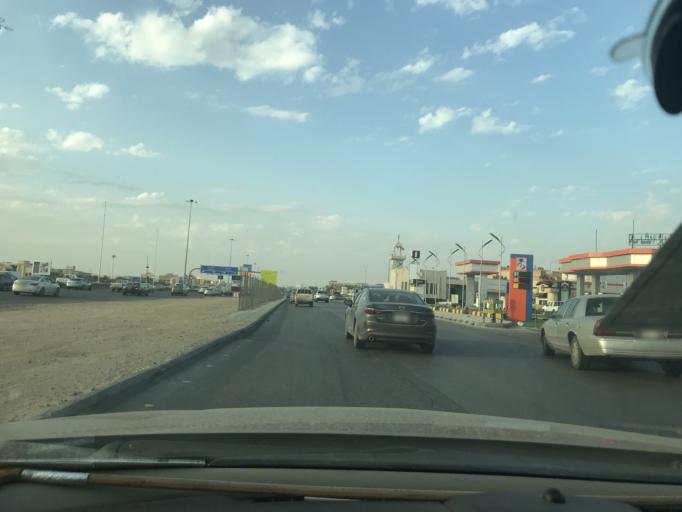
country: SA
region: Ar Riyad
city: Riyadh
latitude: 24.7466
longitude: 46.5853
